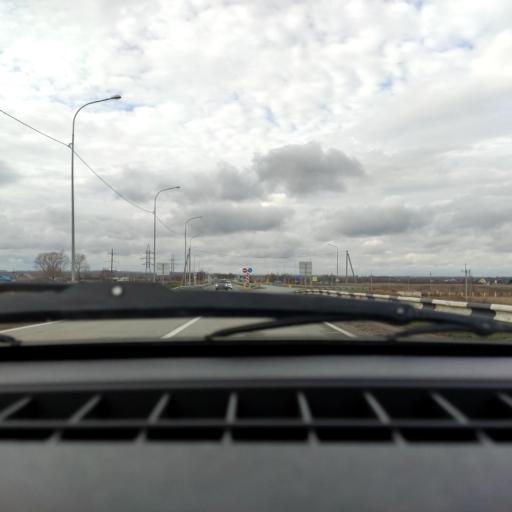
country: RU
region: Bashkortostan
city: Asanovo
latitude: 54.9036
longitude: 55.6243
